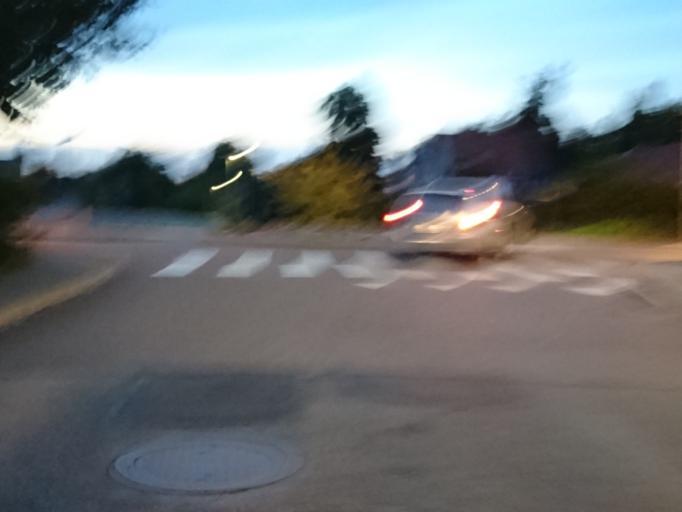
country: SE
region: Stockholm
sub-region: Huddinge Kommun
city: Segeltorp
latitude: 59.2786
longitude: 17.9395
